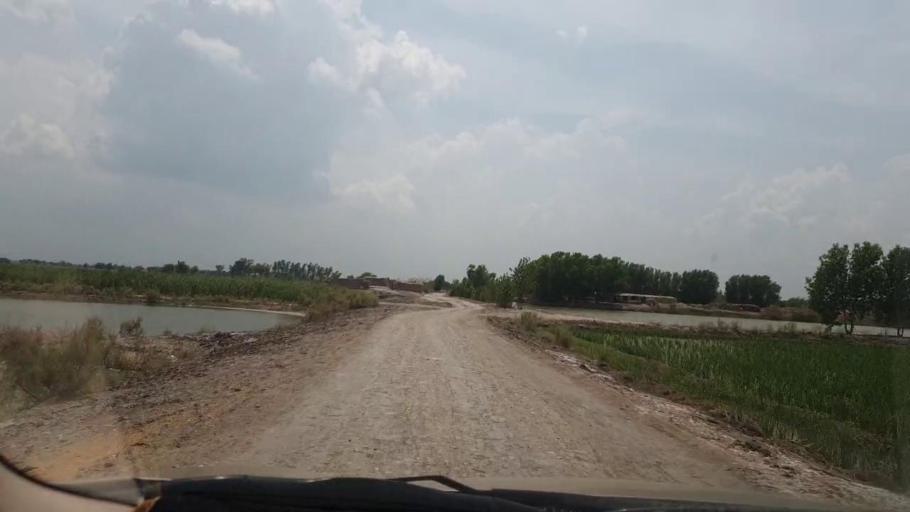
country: PK
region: Sindh
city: Larkana
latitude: 27.6172
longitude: 68.1547
